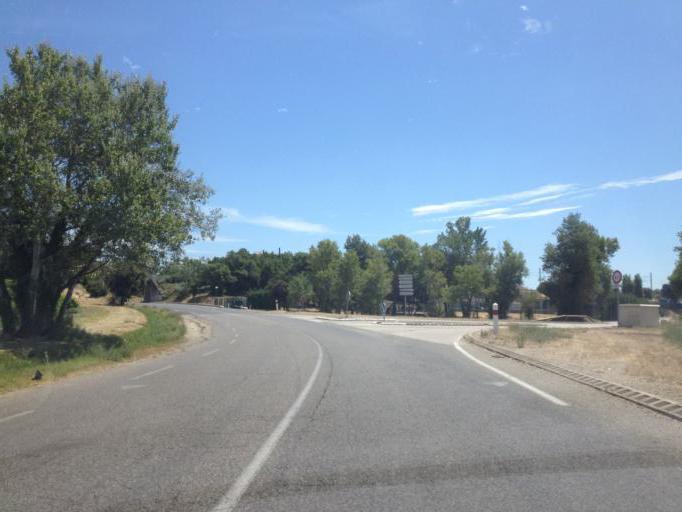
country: FR
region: Provence-Alpes-Cote d'Azur
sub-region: Departement du Vaucluse
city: Sorgues
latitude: 44.0253
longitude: 4.8822
